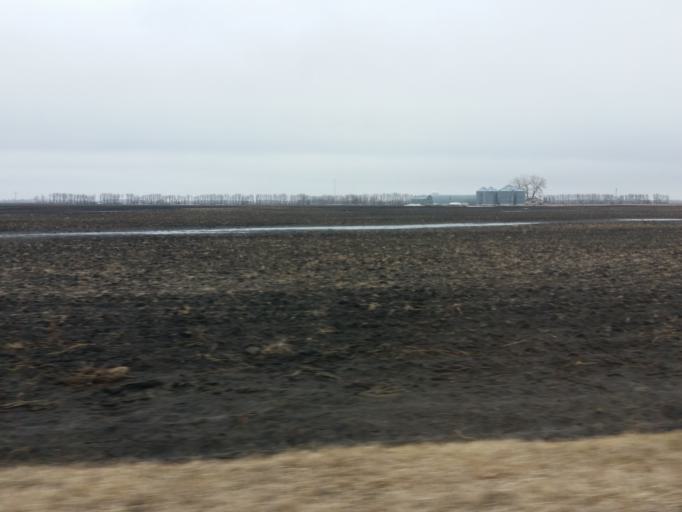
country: US
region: North Dakota
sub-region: Walsh County
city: Grafton
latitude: 48.3592
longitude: -97.2111
